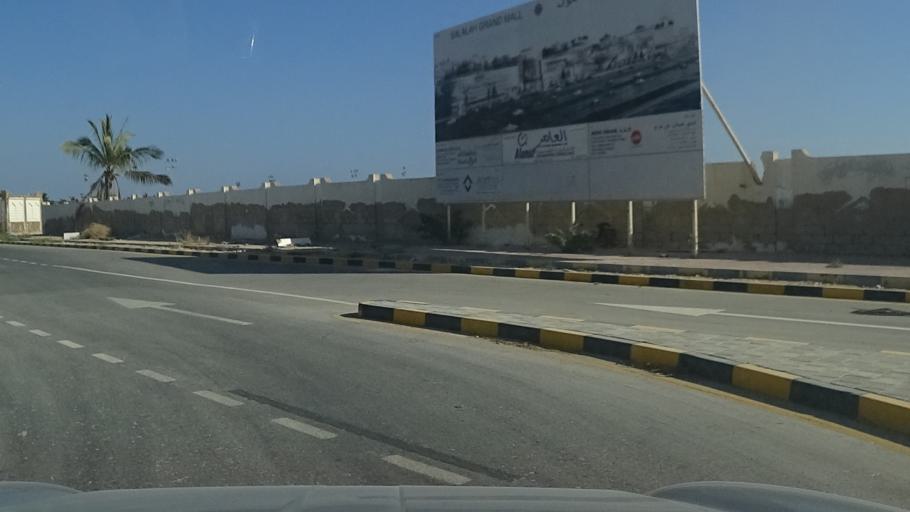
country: OM
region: Zufar
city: Salalah
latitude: 17.0358
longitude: 54.1659
